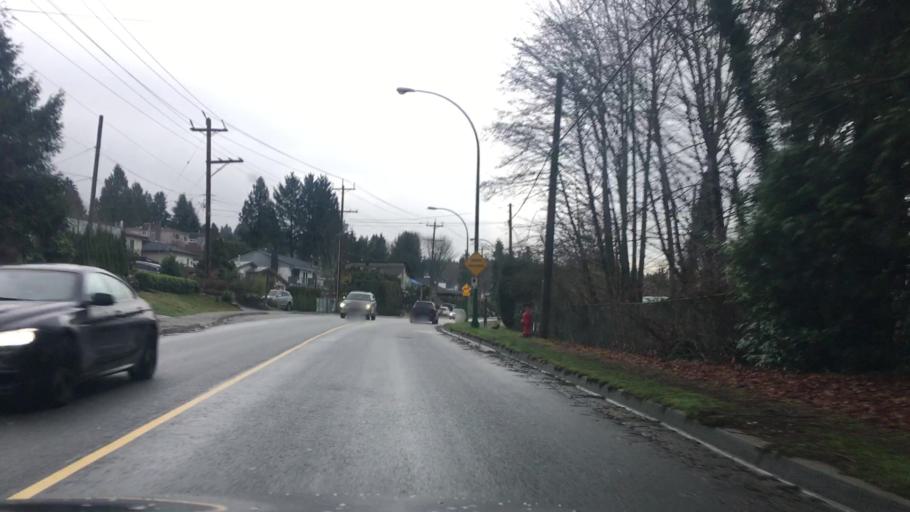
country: CA
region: British Columbia
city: Burnaby
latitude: 49.3087
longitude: -122.9976
